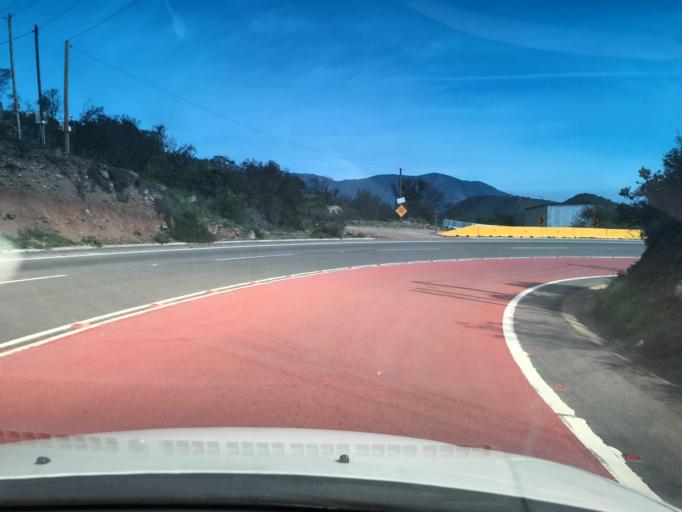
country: CL
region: Valparaiso
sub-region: Provincia de Marga Marga
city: Limache
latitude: -33.0601
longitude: -71.0405
